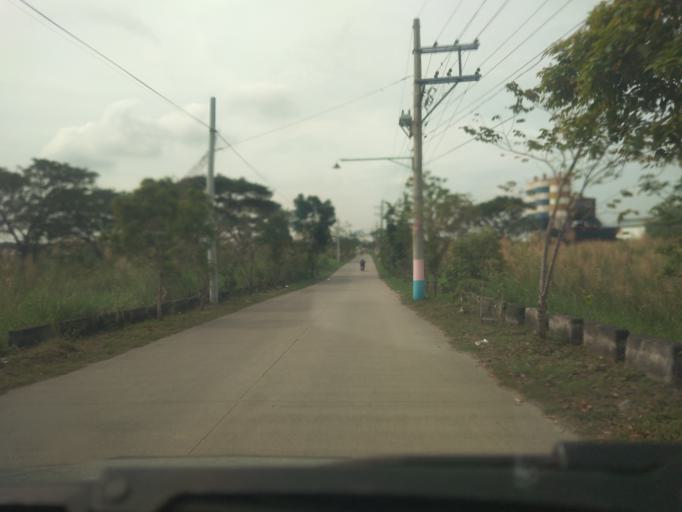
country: PH
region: Central Luzon
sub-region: Province of Pampanga
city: Pau
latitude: 15.0159
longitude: 120.7162
